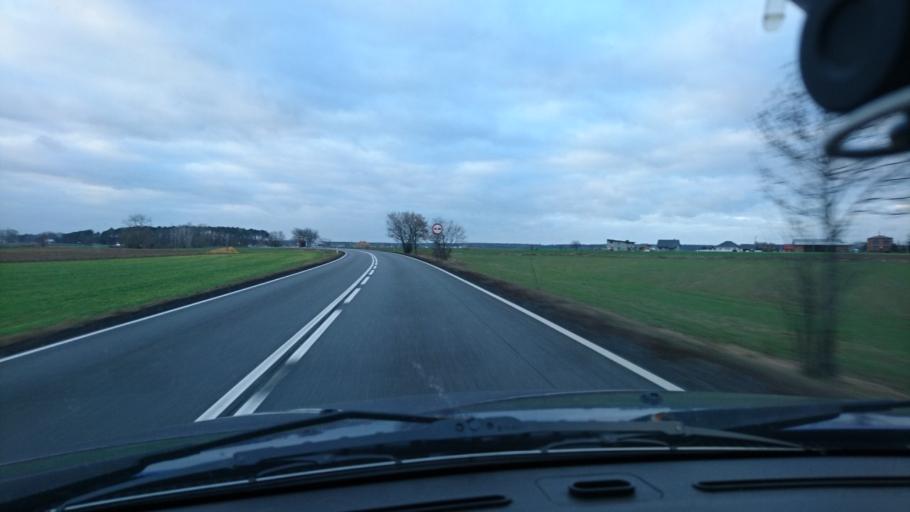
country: PL
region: Greater Poland Voivodeship
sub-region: Powiat kepinski
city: Opatow
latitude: 51.2190
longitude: 18.1377
